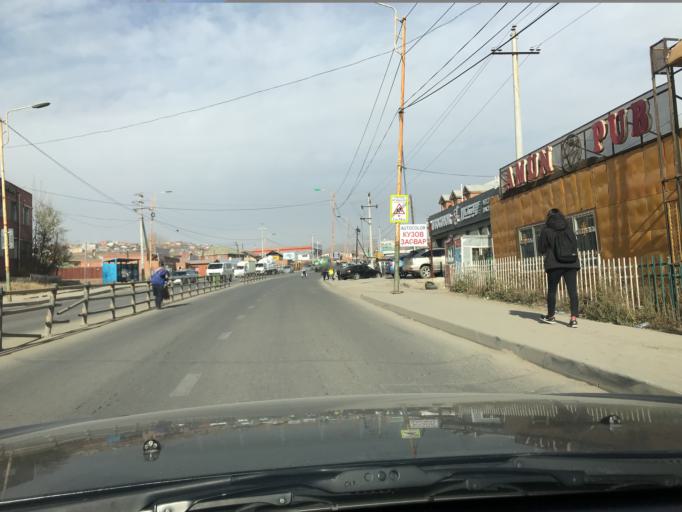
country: MN
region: Ulaanbaatar
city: Ulaanbaatar
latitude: 47.9304
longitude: 106.8886
